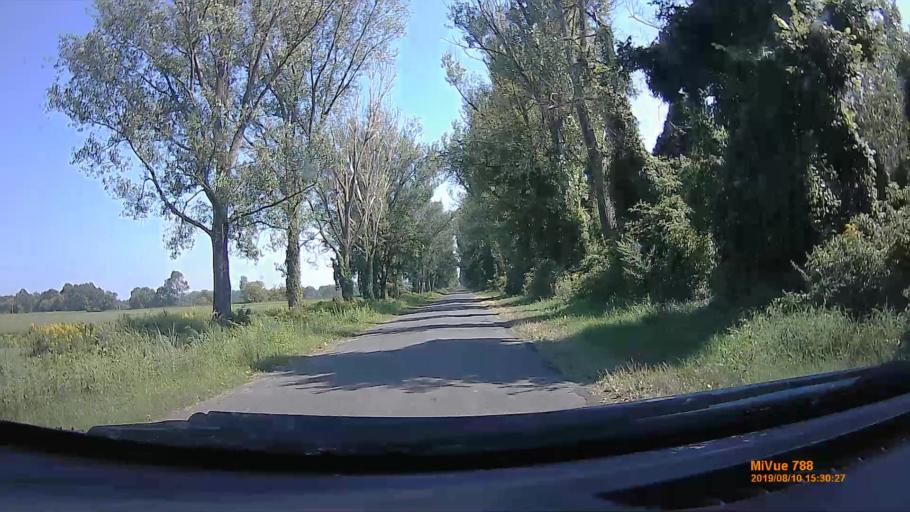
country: HU
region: Somogy
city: Balatonfenyves
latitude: 46.6983
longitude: 17.4873
